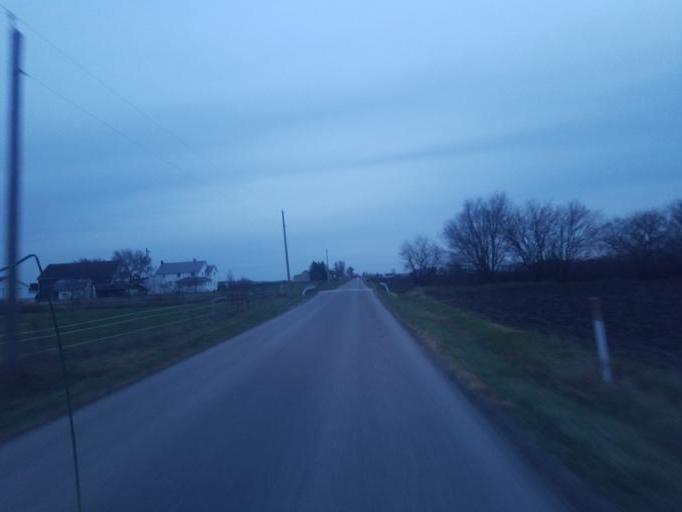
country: US
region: Indiana
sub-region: Adams County
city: Berne
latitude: 40.7290
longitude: -84.8984
